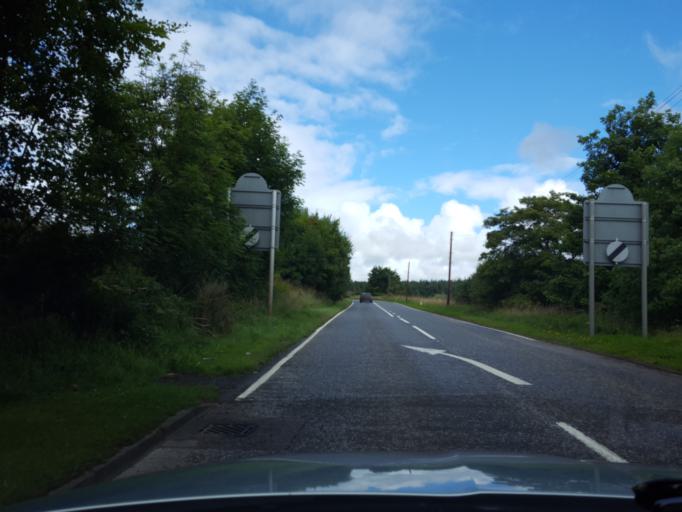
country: GB
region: Scotland
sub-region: Moray
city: Rothes
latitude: 57.5333
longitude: -3.2096
